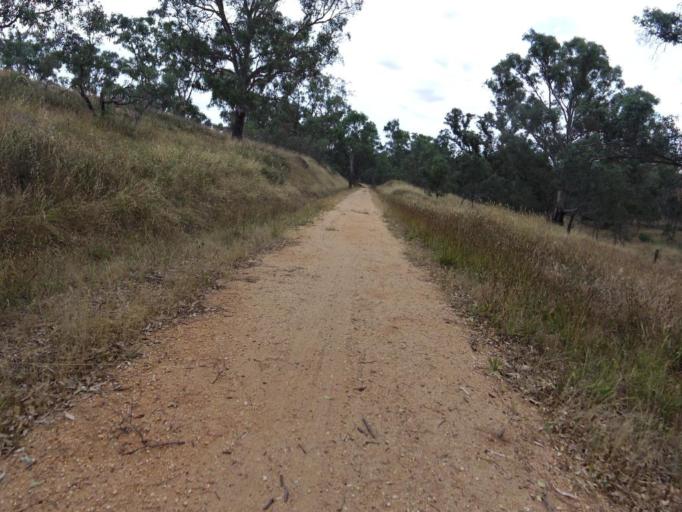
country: AU
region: Victoria
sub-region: Greater Bendigo
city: Kennington
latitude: -36.8638
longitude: 144.6230
